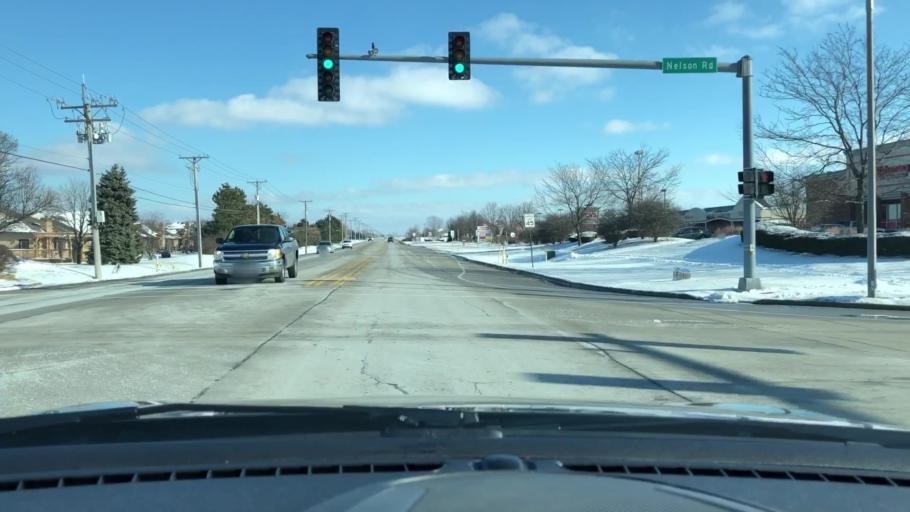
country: US
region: Illinois
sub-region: Will County
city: New Lenox
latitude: 41.4828
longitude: -87.9841
